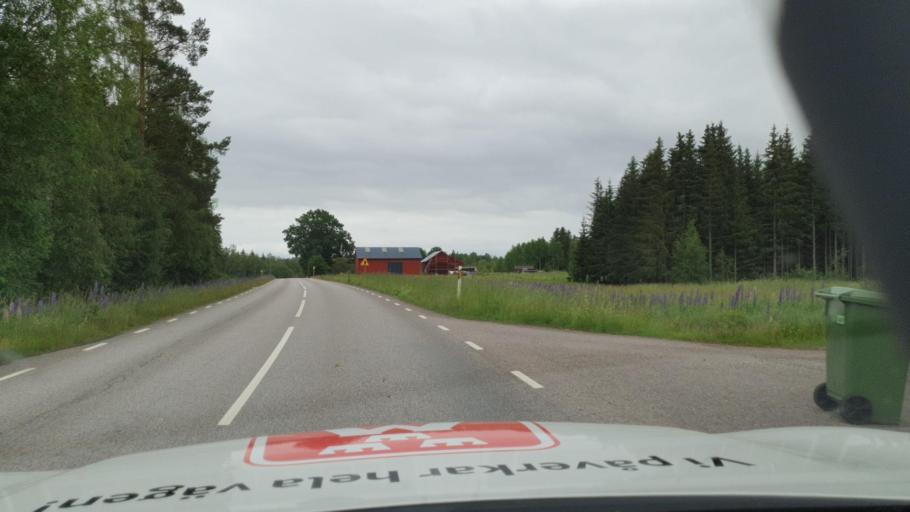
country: SE
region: Vaermland
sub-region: Sunne Kommun
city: Sunne
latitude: 59.7932
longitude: 13.0731
